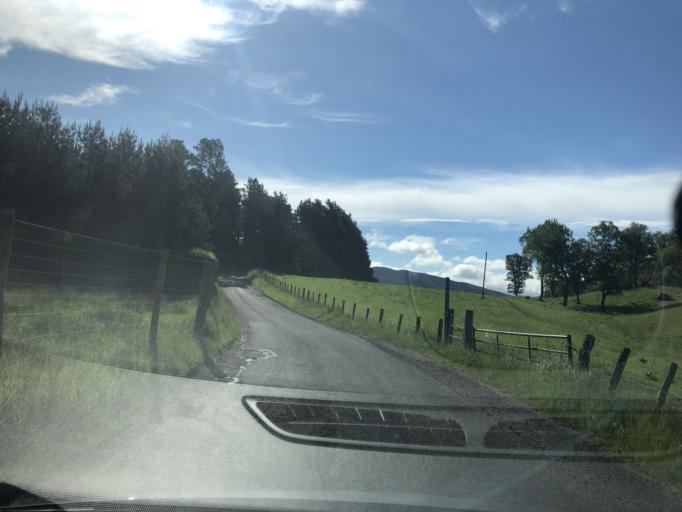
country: GB
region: Scotland
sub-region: Angus
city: Kirriemuir
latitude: 56.8370
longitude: -3.0847
